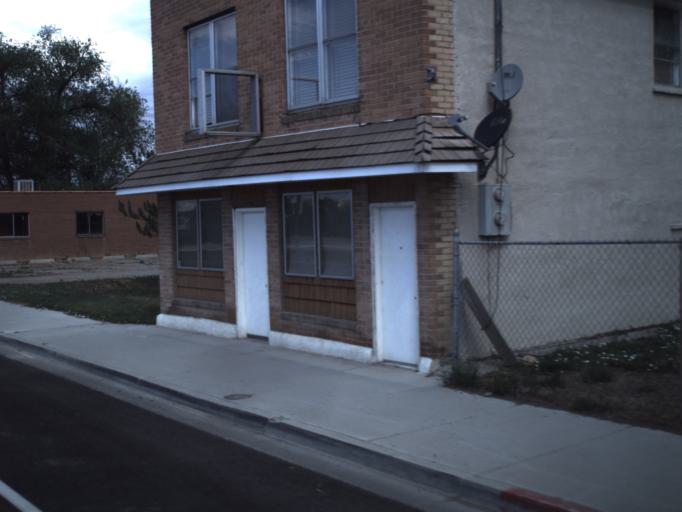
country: US
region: Utah
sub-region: Carbon County
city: Wellington
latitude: 39.5425
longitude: -110.7361
